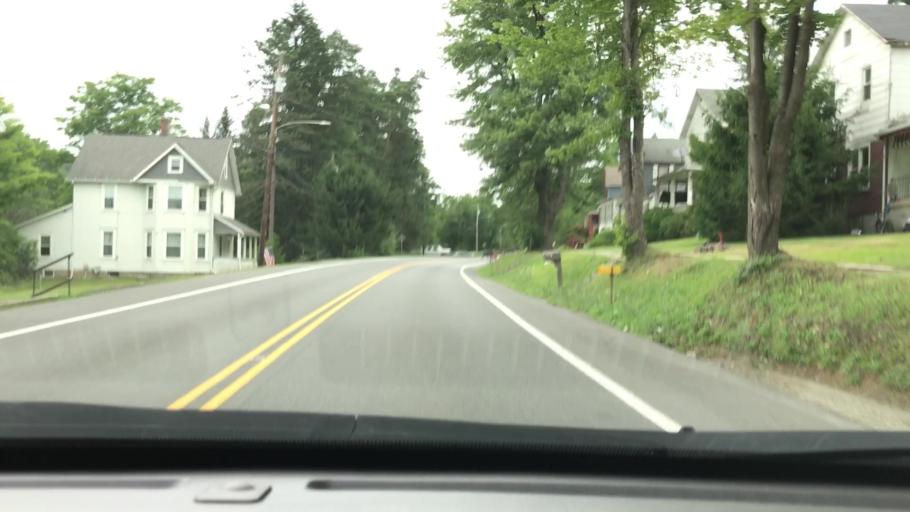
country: US
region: Pennsylvania
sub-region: Elk County
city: Johnsonburg
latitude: 41.5797
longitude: -78.6885
